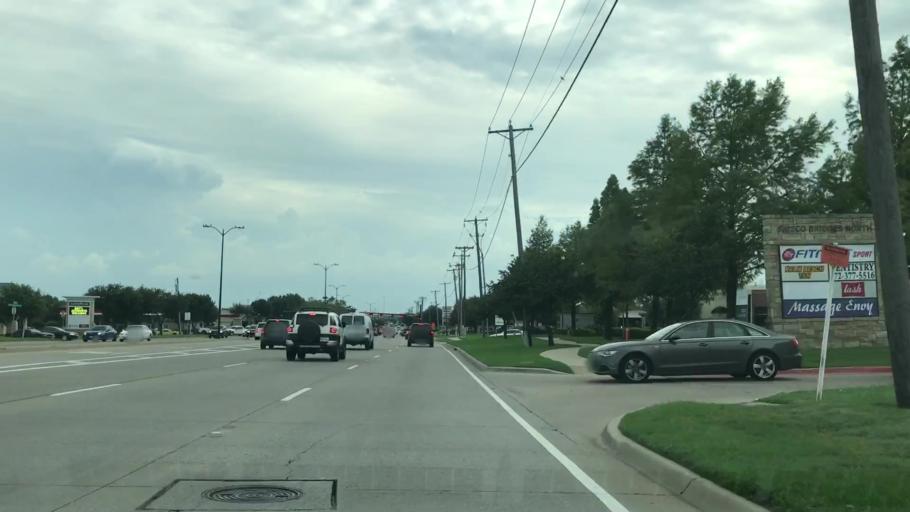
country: US
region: Texas
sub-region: Collin County
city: Frisco
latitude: 33.1114
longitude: -96.8058
